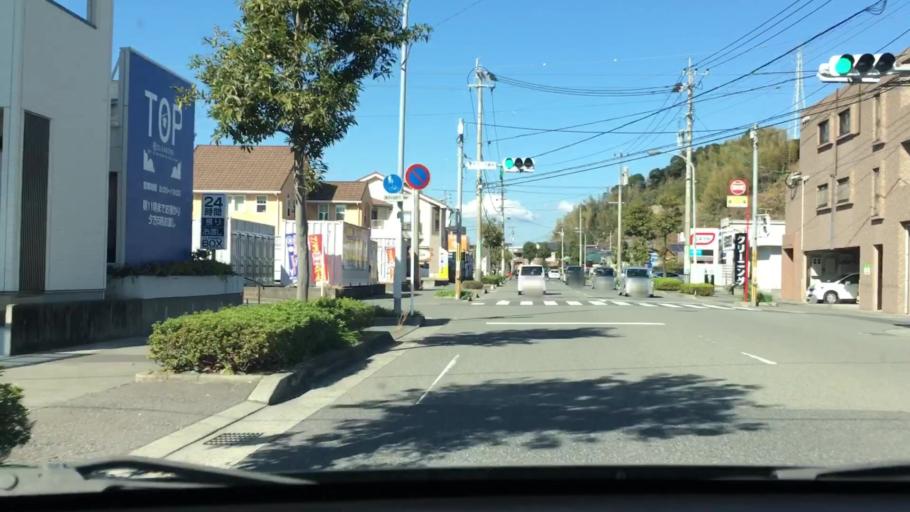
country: JP
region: Kagoshima
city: Kagoshima-shi
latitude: 31.5510
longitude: 130.5301
